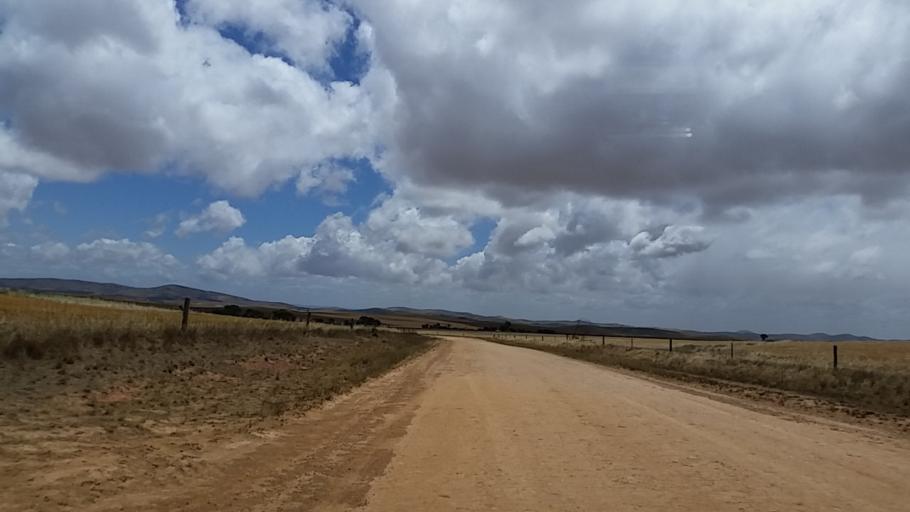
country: AU
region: South Australia
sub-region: Peterborough
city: Peterborough
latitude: -32.8610
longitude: 138.6183
